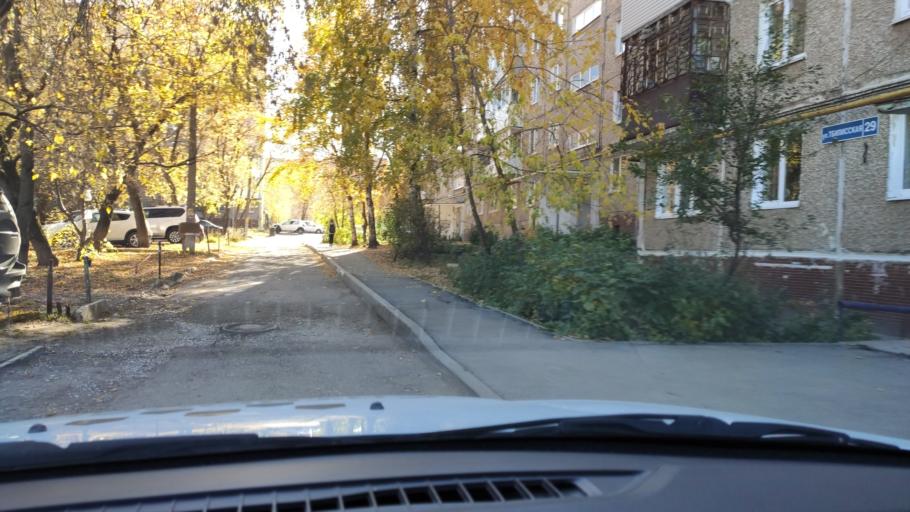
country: RU
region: Perm
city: Perm
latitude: 57.9669
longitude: 56.2131
